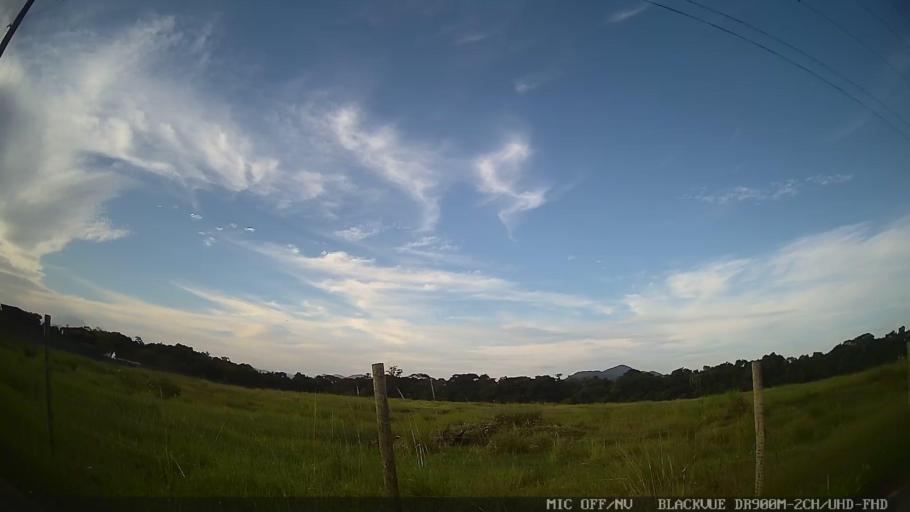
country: BR
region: Sao Paulo
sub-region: Itanhaem
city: Itanhaem
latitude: -24.1521
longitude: -46.7911
